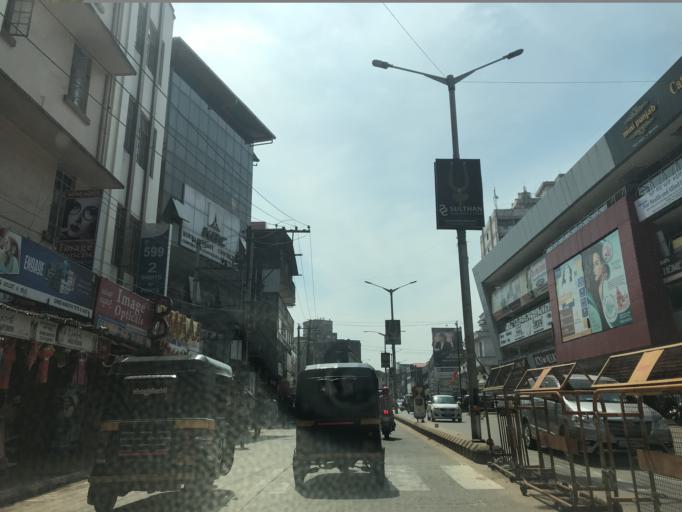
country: IN
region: Karnataka
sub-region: Dakshina Kannada
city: Mangalore
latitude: 12.8702
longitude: 74.8419
